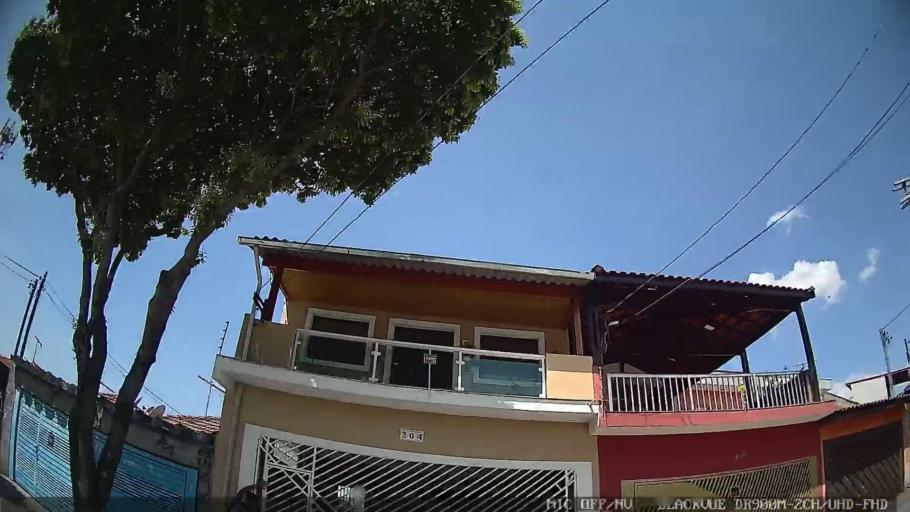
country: BR
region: Sao Paulo
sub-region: Guarulhos
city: Guarulhos
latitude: -23.5038
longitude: -46.5193
